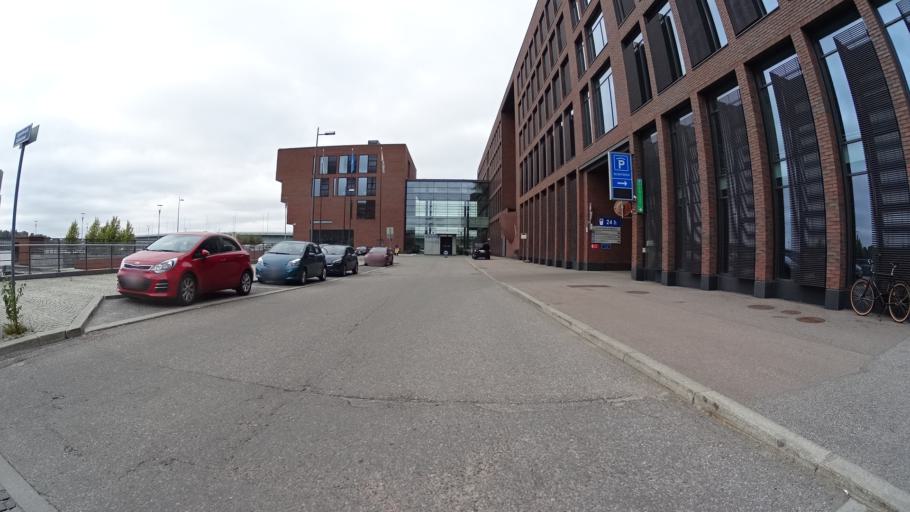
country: FI
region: Uusimaa
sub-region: Helsinki
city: Helsinki
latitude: 60.1656
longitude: 24.9000
